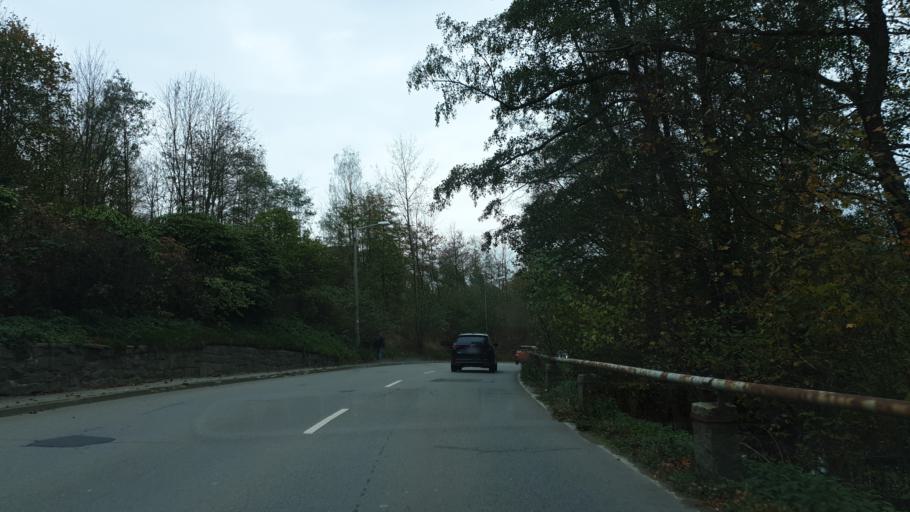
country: DE
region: Saxony
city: Schwarzenberg
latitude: 50.5313
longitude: 12.7864
